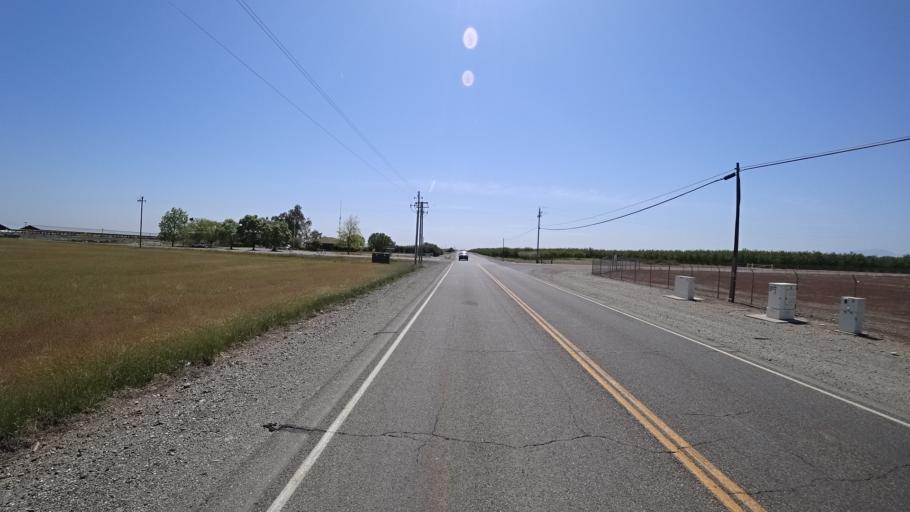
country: US
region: California
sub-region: Glenn County
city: Orland
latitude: 39.6830
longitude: -122.1969
